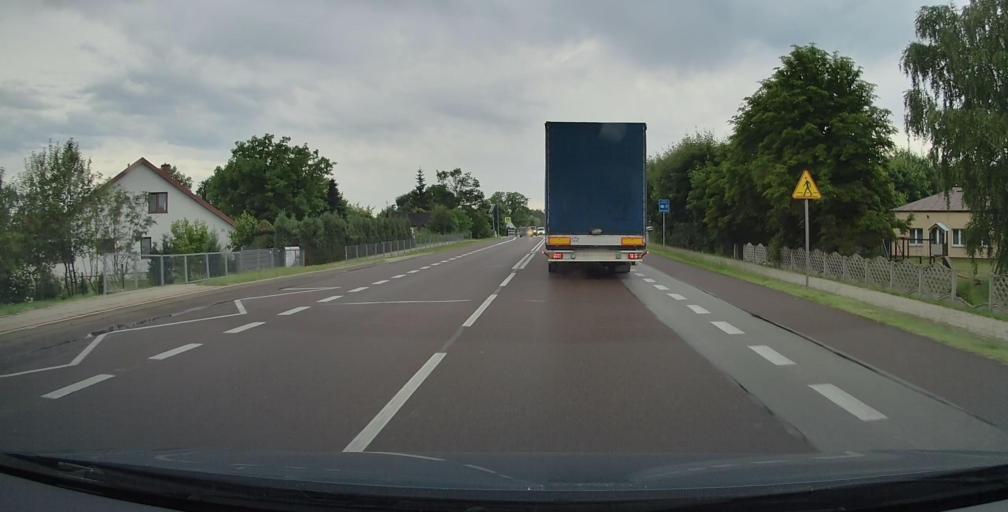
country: PL
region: Lublin Voivodeship
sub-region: Powiat bialski
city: Miedzyrzec Podlaski
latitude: 52.0290
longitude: 22.8831
